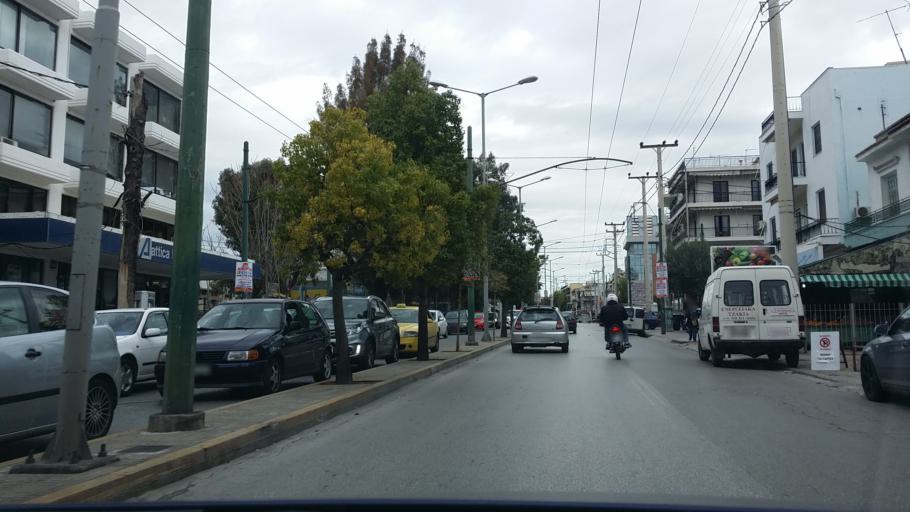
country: GR
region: Attica
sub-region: Nomarchia Athinas
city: Peristeri
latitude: 38.0174
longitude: 23.6921
